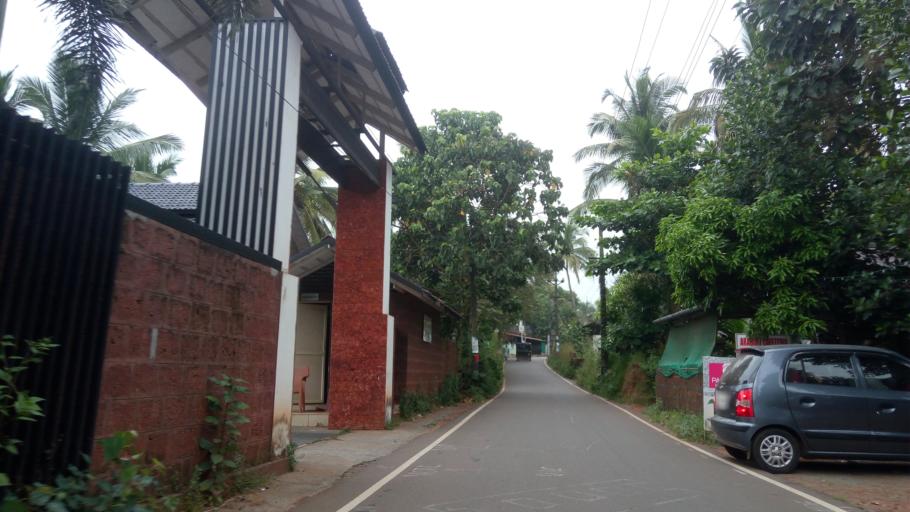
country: IN
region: Kerala
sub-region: Malappuram
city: Malappuram
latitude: 10.9811
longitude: 76.0064
